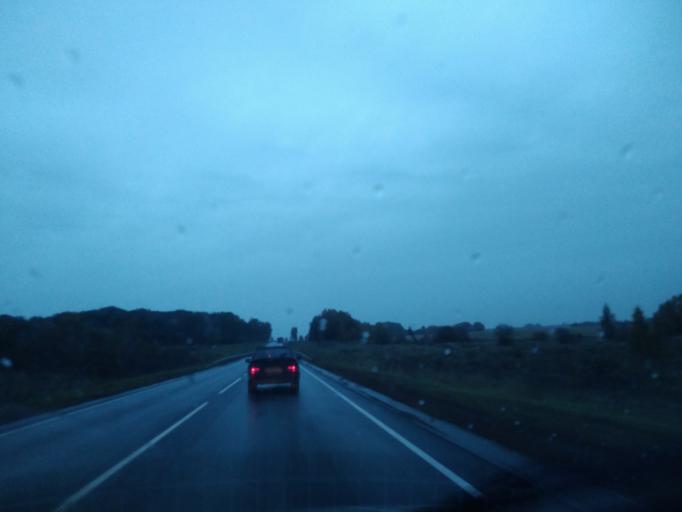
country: RU
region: Tula
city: Teploye
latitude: 53.7387
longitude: 37.4717
